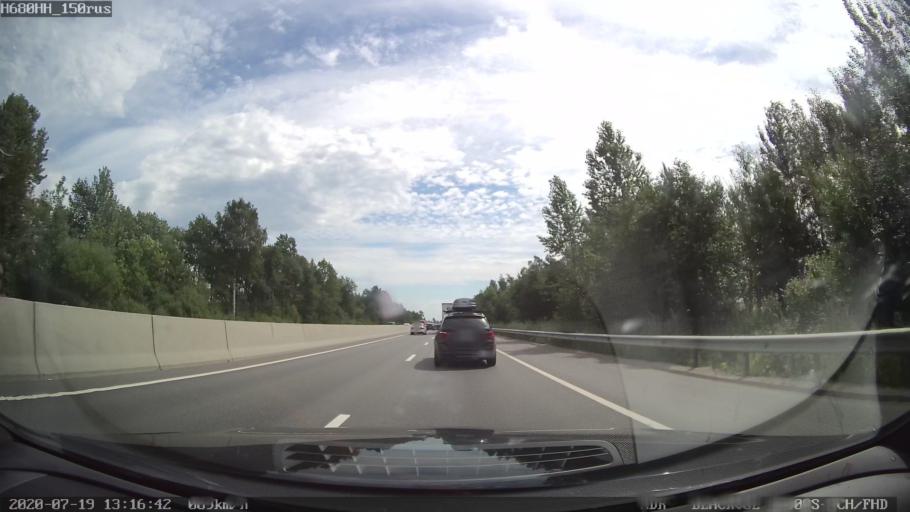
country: RU
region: St.-Petersburg
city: Kolpino
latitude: 59.7151
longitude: 30.5585
